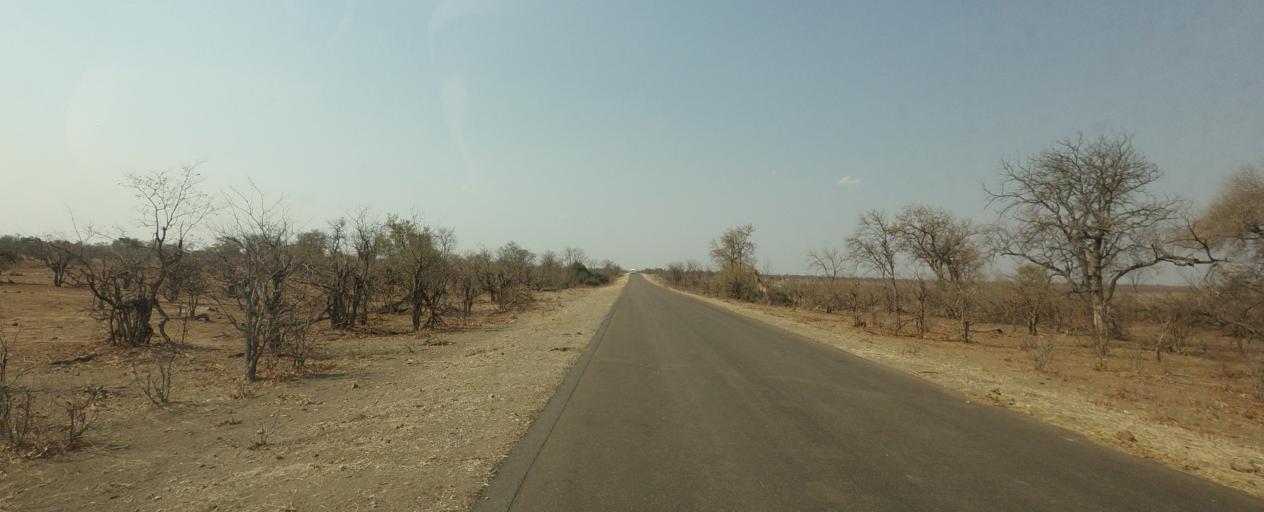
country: ZA
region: Limpopo
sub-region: Mopani District Municipality
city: Giyani
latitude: -23.1308
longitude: 31.3796
